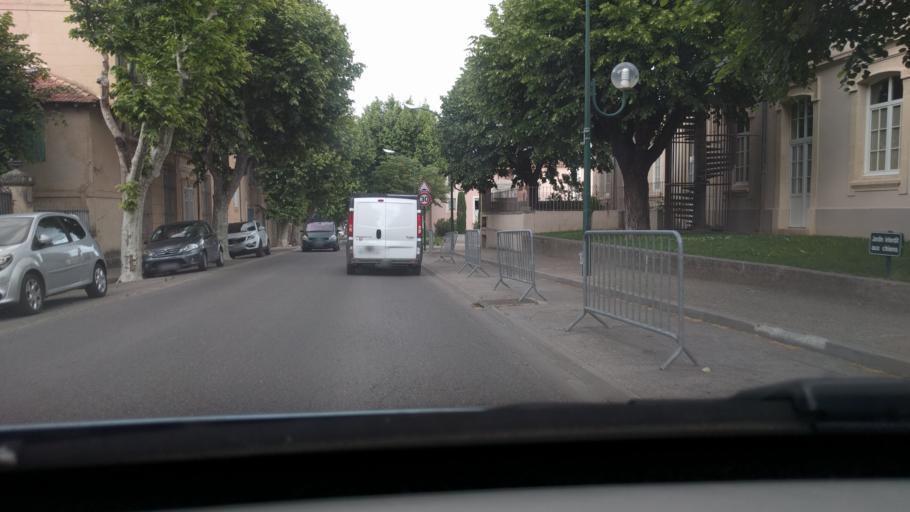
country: FR
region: Provence-Alpes-Cote d'Azur
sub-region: Departement du Vaucluse
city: Grambois
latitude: 43.7275
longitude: 5.5499
